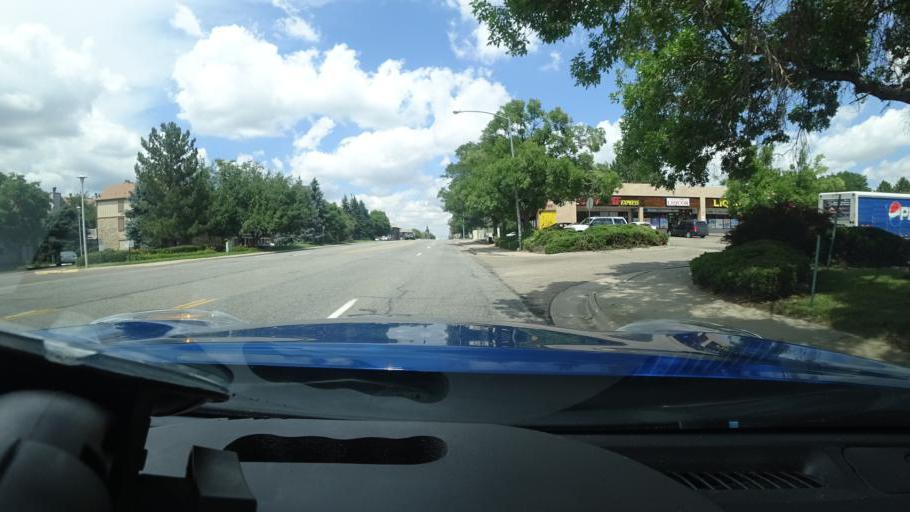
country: US
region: Colorado
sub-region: Adams County
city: Aurora
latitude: 39.6992
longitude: -104.8470
